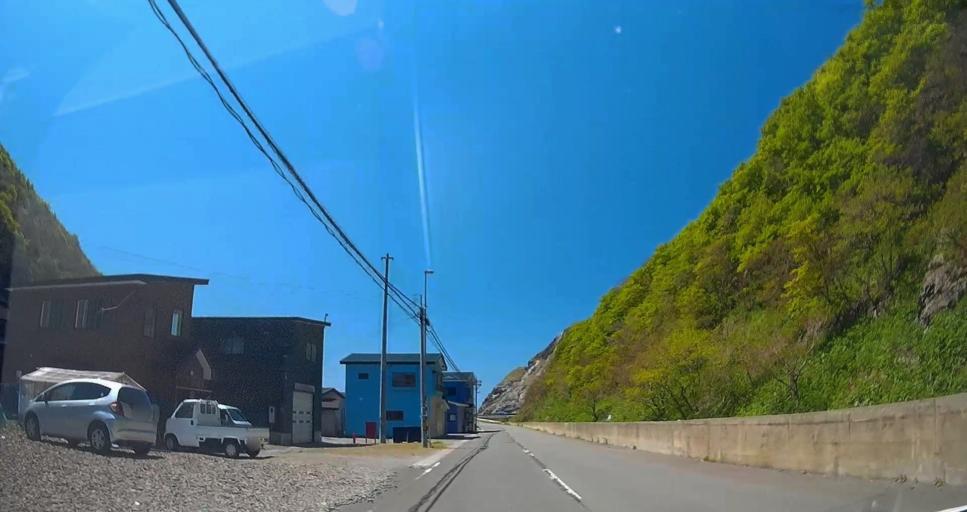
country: JP
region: Aomori
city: Mutsu
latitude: 41.3281
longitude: 140.8101
